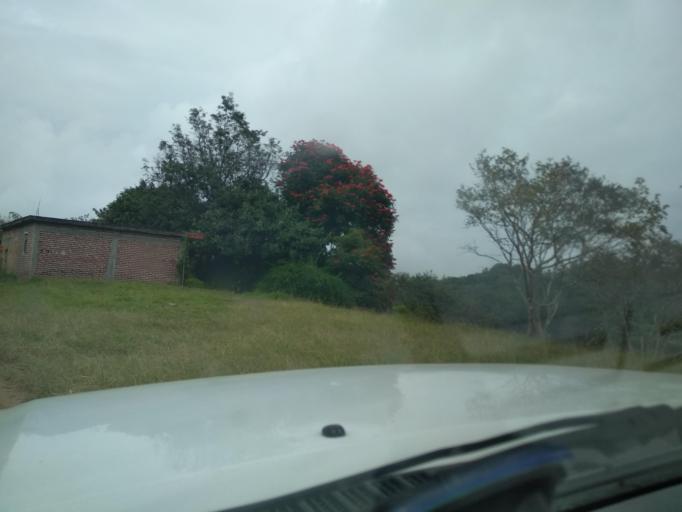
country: MX
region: Veracruz
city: El Castillo
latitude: 19.5404
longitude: -96.8335
